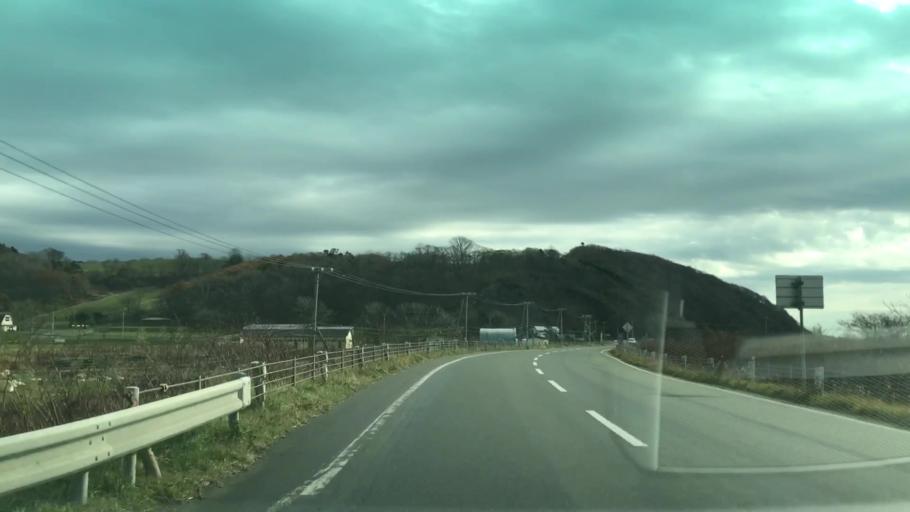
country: JP
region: Hokkaido
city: Shizunai-furukawacho
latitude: 42.1422
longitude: 142.8505
